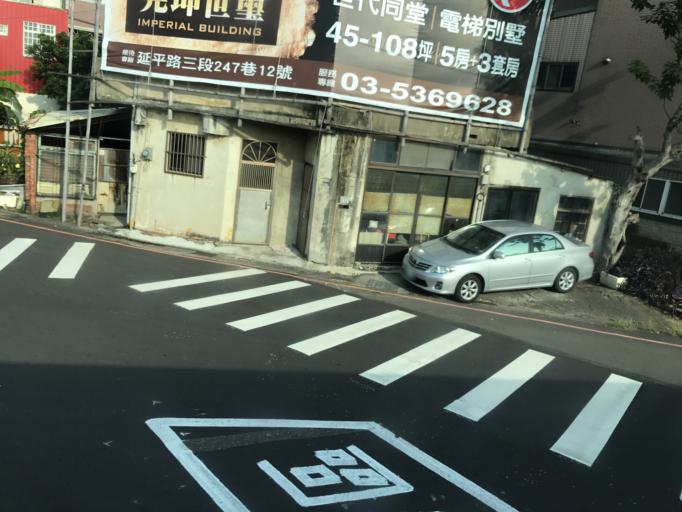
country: TW
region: Taiwan
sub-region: Hsinchu
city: Hsinchu
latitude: 24.8394
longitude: 120.9339
